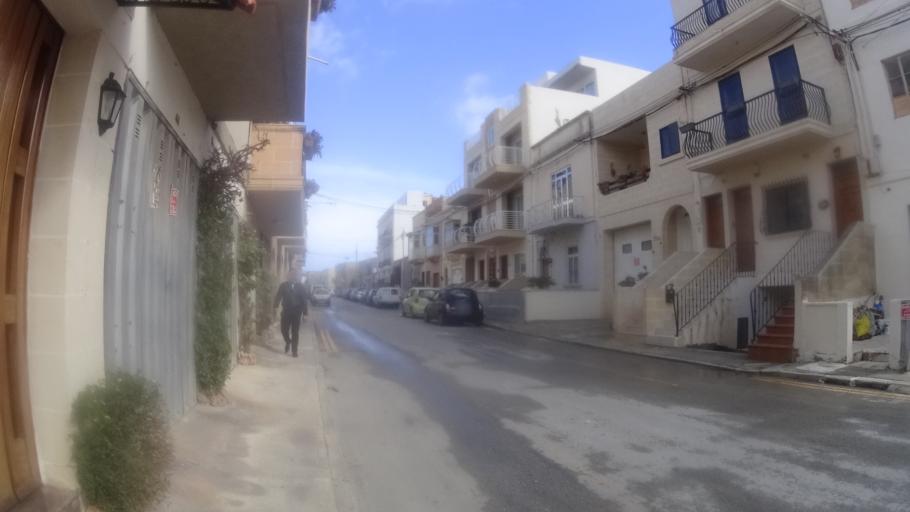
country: MT
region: In-Naxxar
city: Naxxar
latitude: 35.9163
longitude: 14.4464
